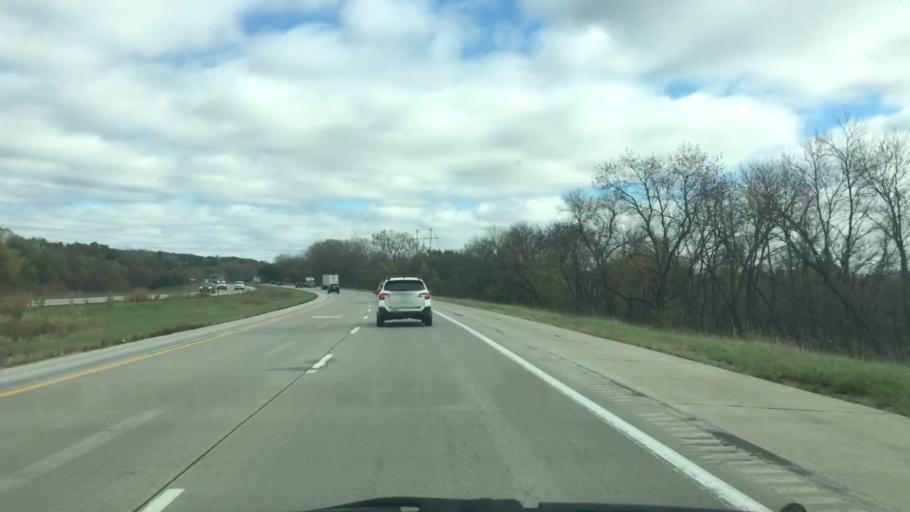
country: US
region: Iowa
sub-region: Jasper County
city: Colfax
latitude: 41.6821
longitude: -93.2990
